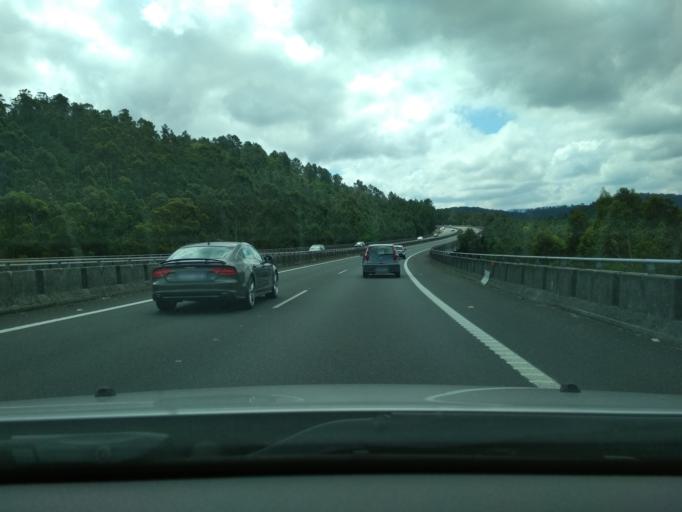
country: ES
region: Galicia
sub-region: Provincia de Pontevedra
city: Portas
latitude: 42.5881
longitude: -8.6758
